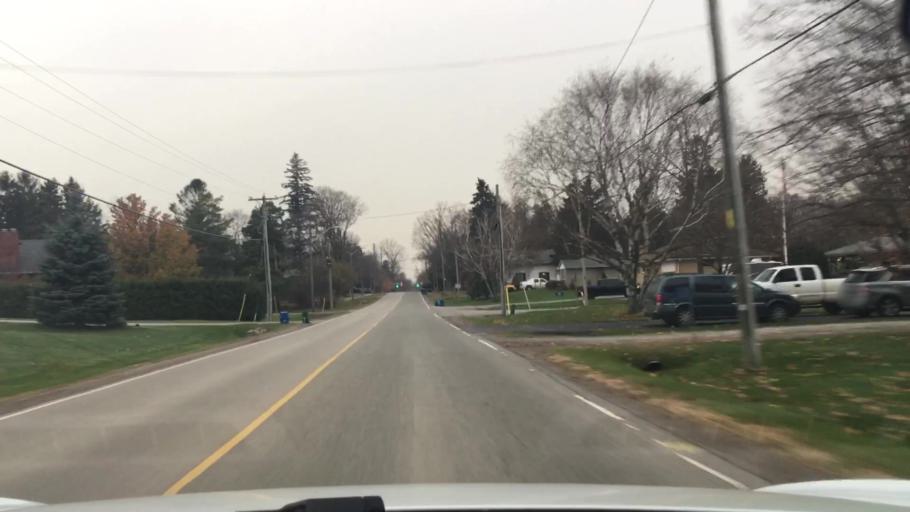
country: CA
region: Ontario
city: Oshawa
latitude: 43.9836
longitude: -78.9070
